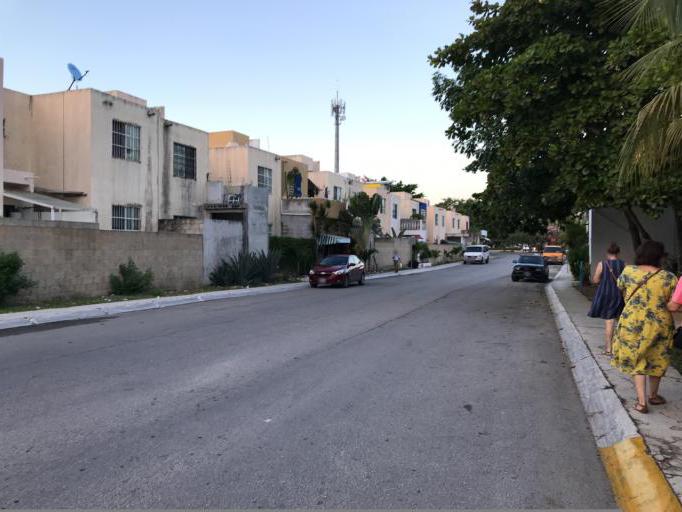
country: MX
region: Quintana Roo
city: Playa del Carmen
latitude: 20.6578
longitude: -87.0681
